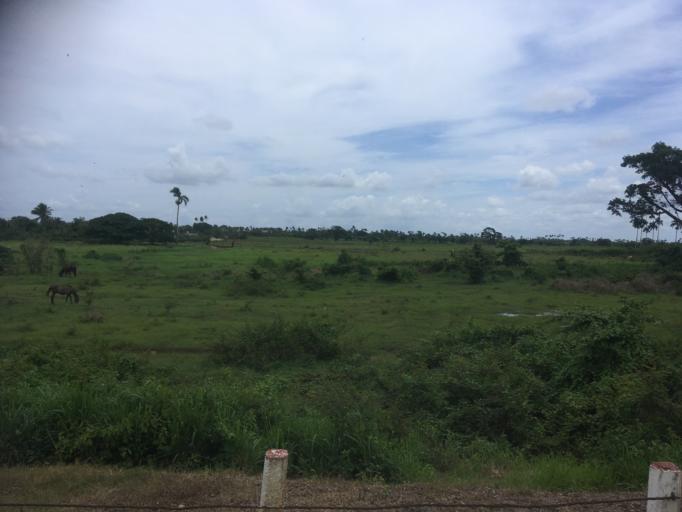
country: CU
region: Matanzas
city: Colon
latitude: 22.7131
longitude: -80.8973
